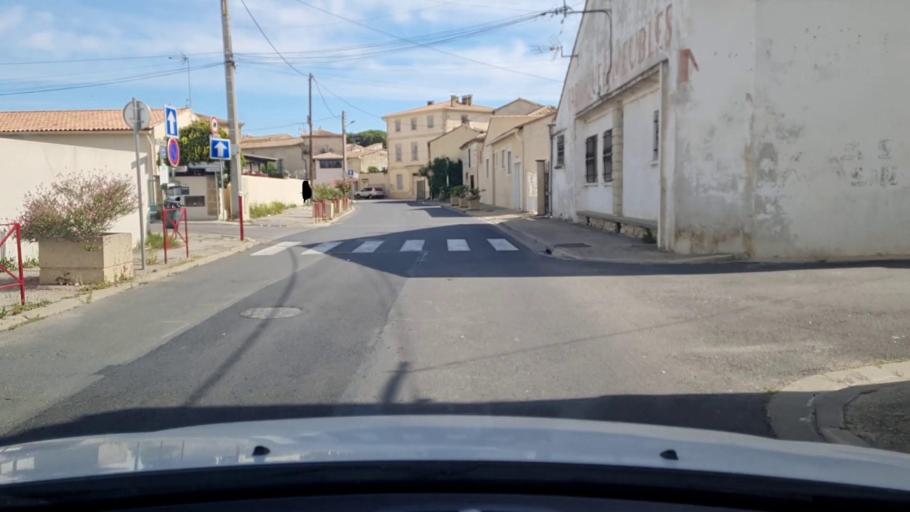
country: FR
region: Languedoc-Roussillon
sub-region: Departement de l'Herault
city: Marsillargues
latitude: 43.6317
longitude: 4.1969
